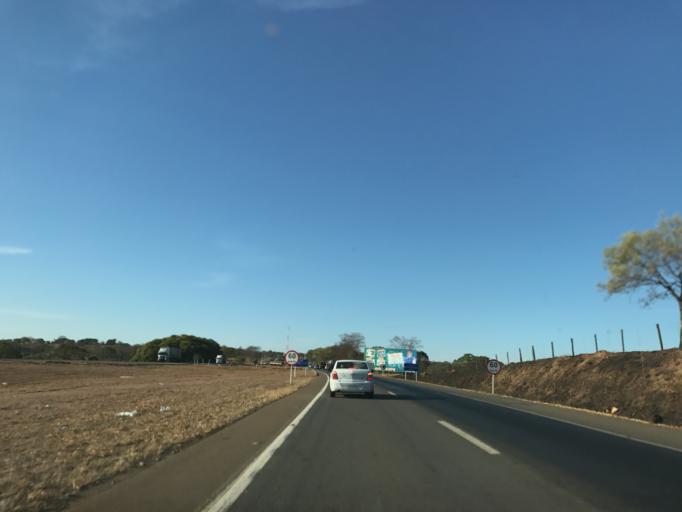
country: BR
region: Goias
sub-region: Hidrolandia
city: Hidrolandia
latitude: -16.9164
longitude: -49.2535
